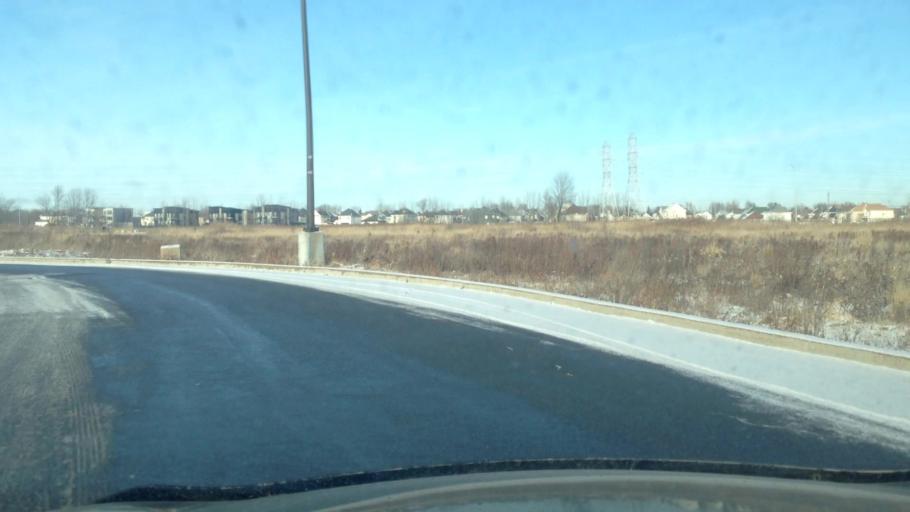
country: CA
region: Quebec
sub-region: Monteregie
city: Mercier
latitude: 45.3450
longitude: -73.7560
